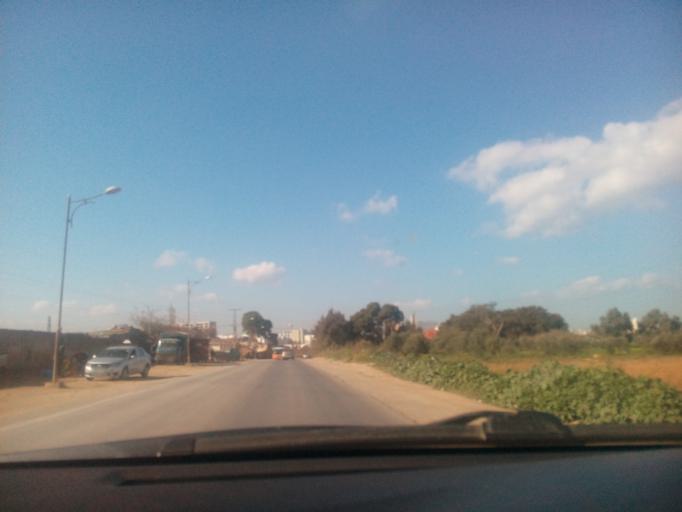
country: DZ
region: Oran
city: Es Senia
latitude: 35.6757
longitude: -0.5936
